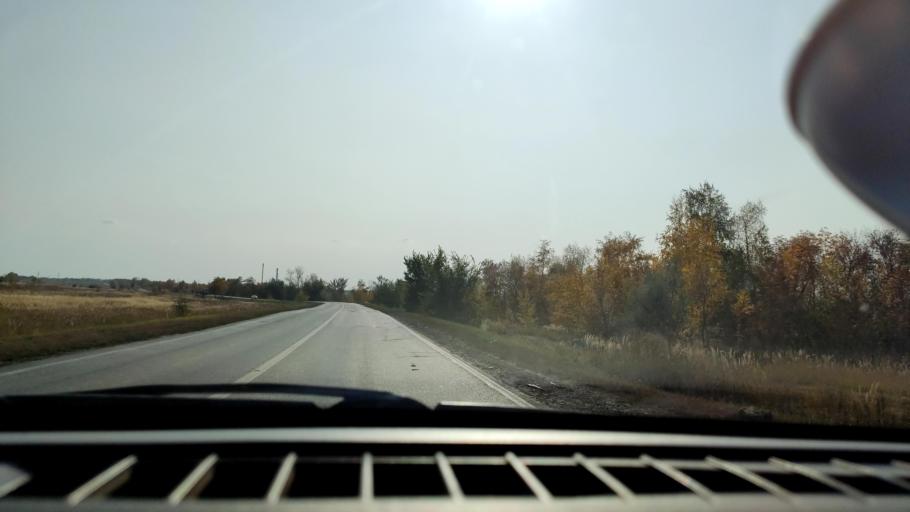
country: RU
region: Samara
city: Smyshlyayevka
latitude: 53.1071
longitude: 50.3511
